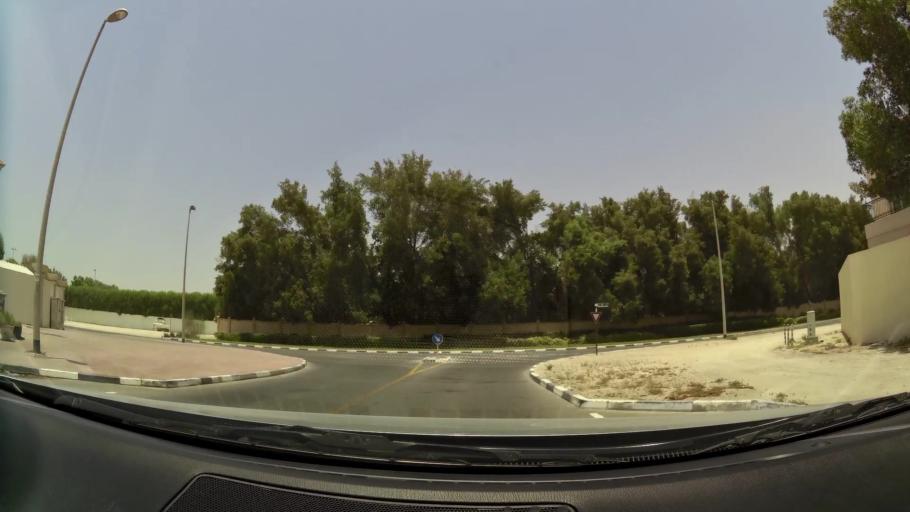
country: AE
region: Dubai
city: Dubai
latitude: 25.1741
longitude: 55.2399
